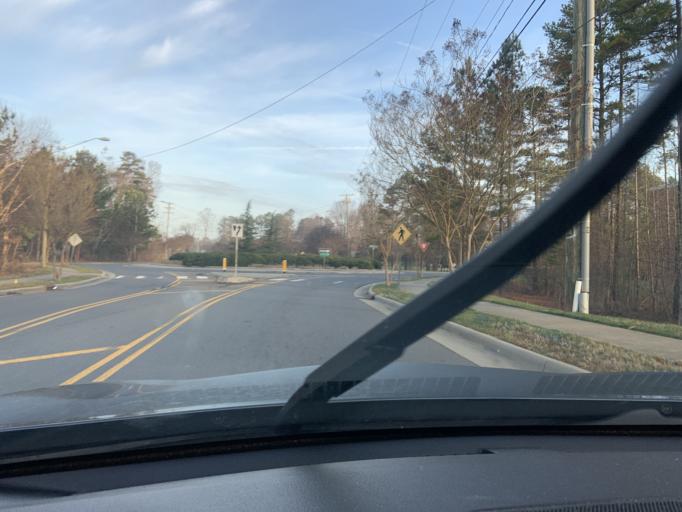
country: US
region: North Carolina
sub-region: Mecklenburg County
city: Charlotte
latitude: 35.2318
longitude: -80.9168
